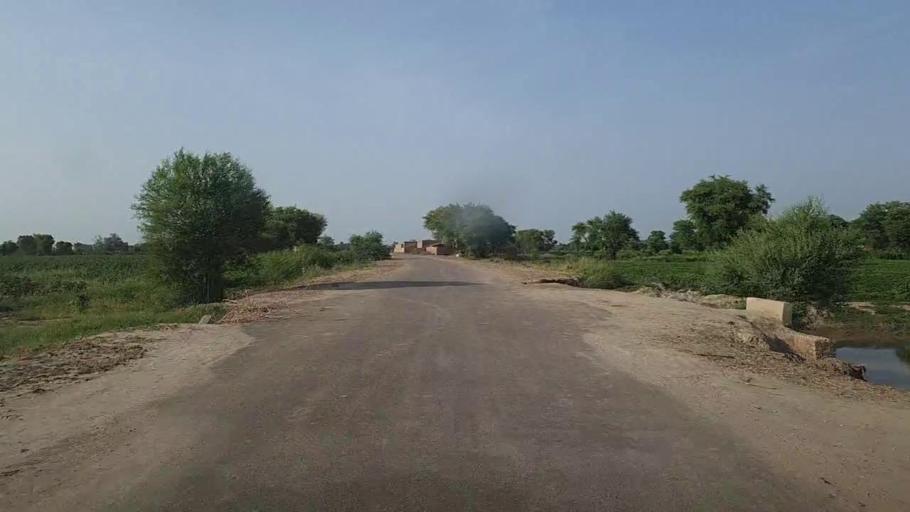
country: PK
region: Sindh
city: Ubauro
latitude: 28.0953
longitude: 69.8454
